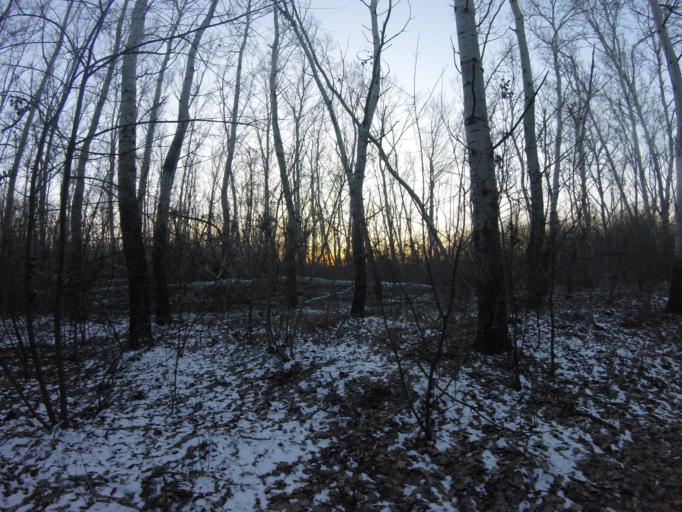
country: HU
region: Budapest
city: Budapest XVII. keruelet
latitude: 47.4492
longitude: 19.2768
